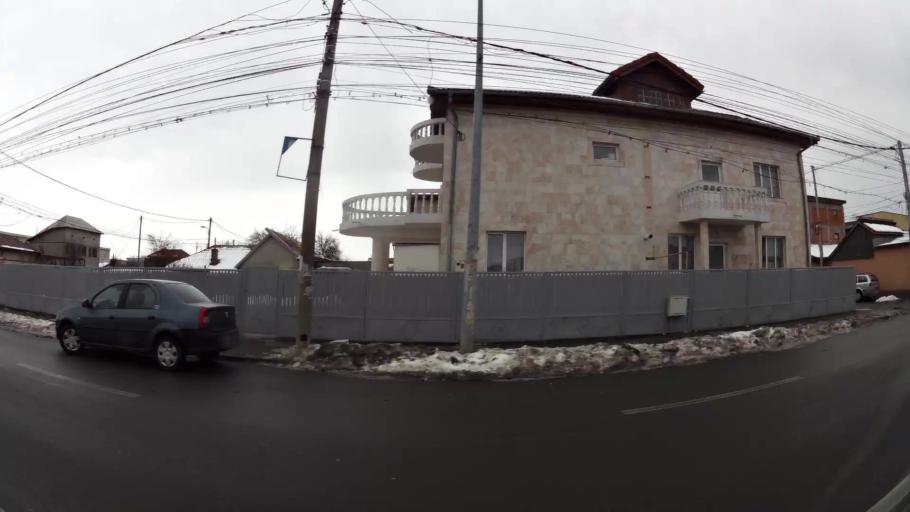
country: RO
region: Ilfov
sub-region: Comuna Pantelimon
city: Pantelimon
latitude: 44.4285
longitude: 26.2084
